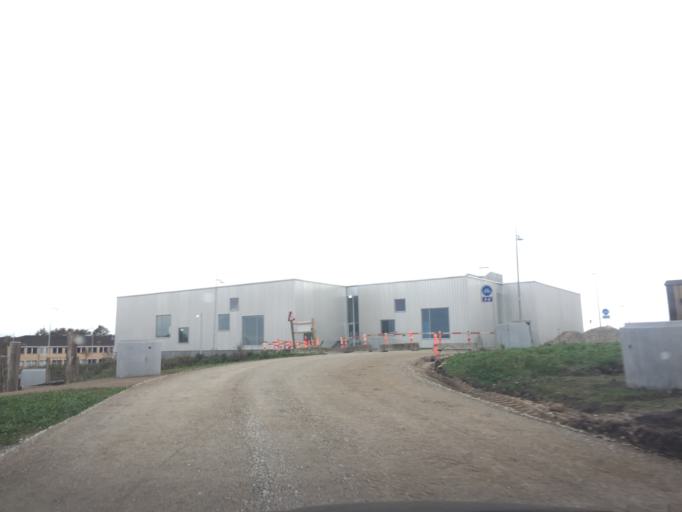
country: DK
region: Capital Region
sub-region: Hoje-Taastrup Kommune
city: Flong
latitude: 55.6450
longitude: 12.2060
